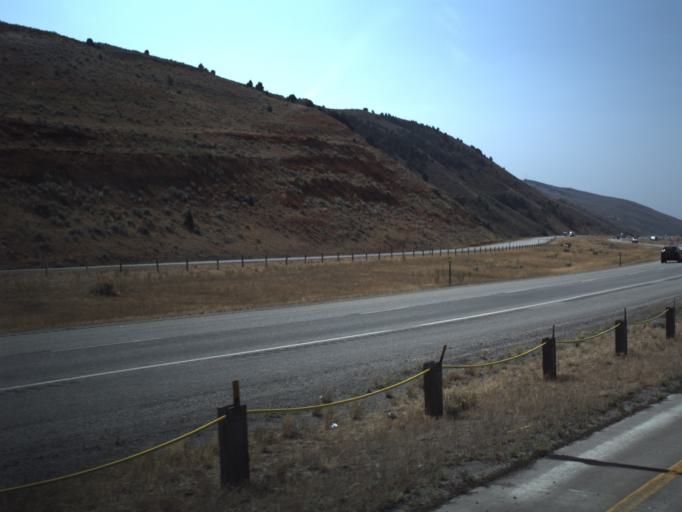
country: US
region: Utah
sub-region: Summit County
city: Coalville
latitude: 41.0850
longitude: -111.2386
